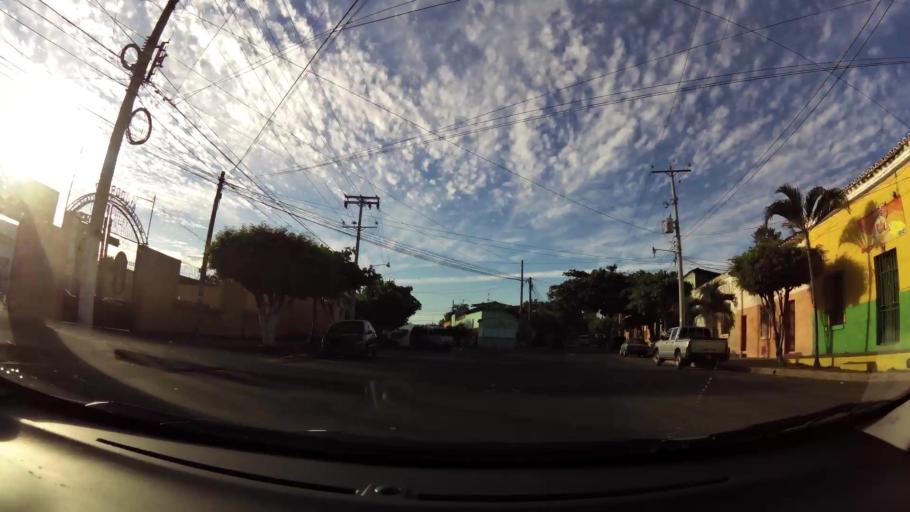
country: SV
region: Santa Ana
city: Santa Ana
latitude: 13.9894
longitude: -89.5478
